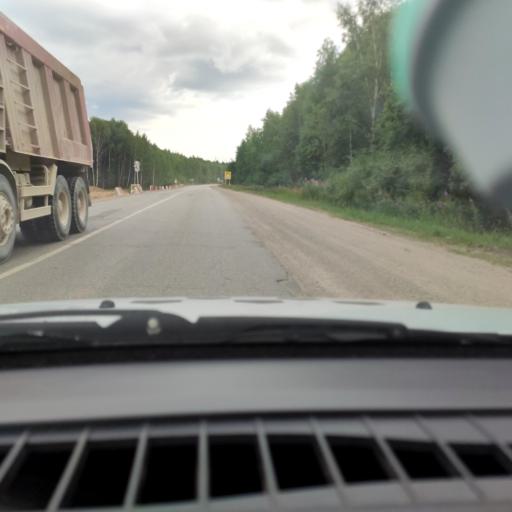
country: RU
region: Perm
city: Solikamsk
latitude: 59.5621
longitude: 56.7784
